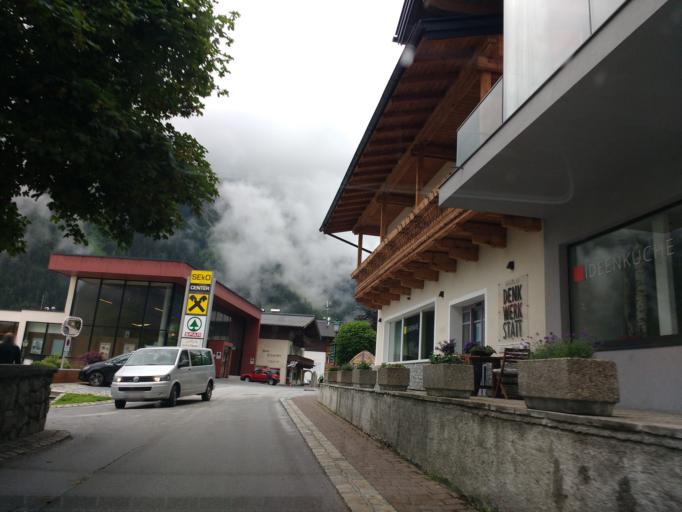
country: AT
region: Salzburg
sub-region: Politischer Bezirk Zell am See
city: Krimml
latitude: 47.2218
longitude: 12.1745
